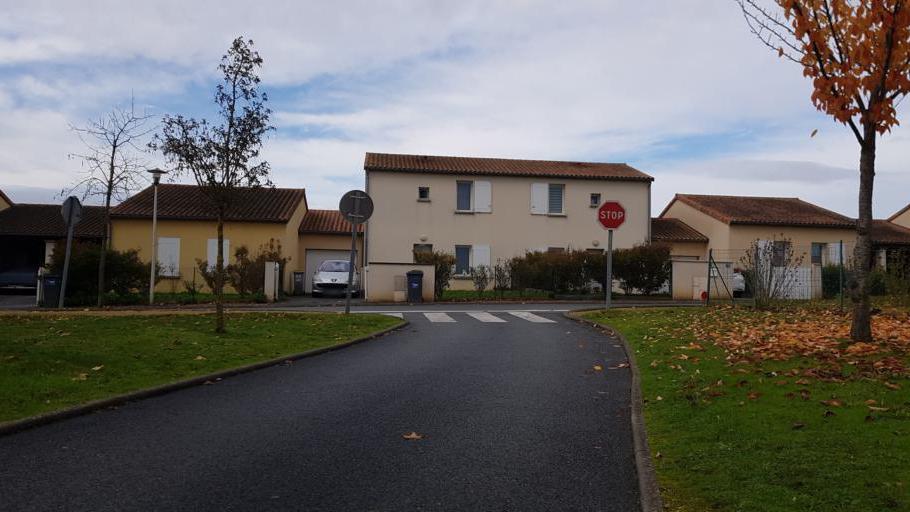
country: FR
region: Poitou-Charentes
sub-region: Departement de la Vienne
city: Chasseneuil-du-Poitou
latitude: 46.6438
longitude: 0.3574
